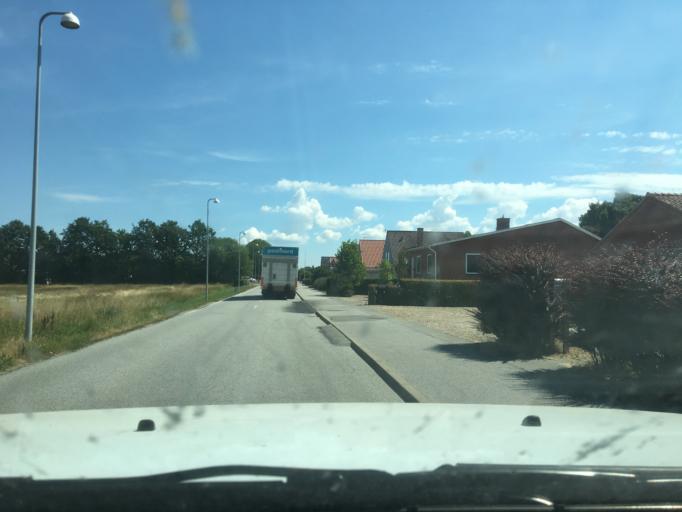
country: DK
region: Central Jutland
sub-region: Randers Kommune
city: Assentoft
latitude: 56.3649
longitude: 10.1586
